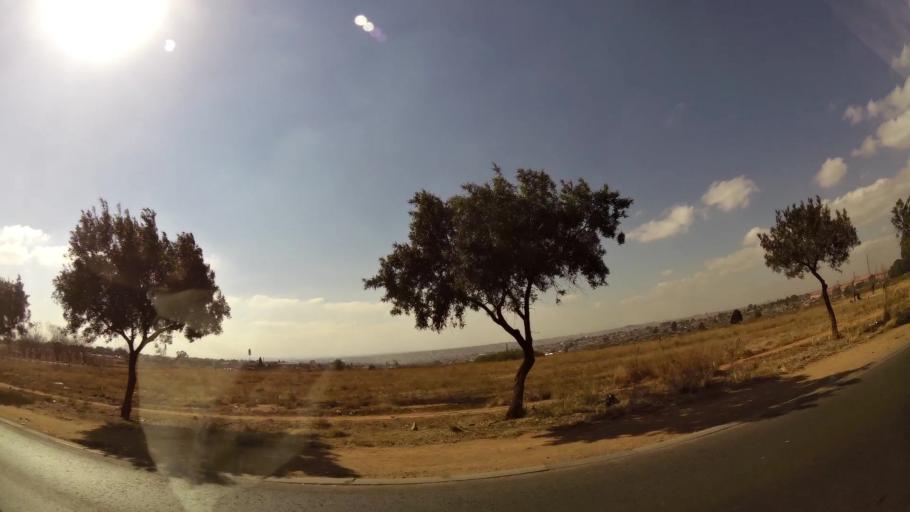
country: ZA
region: Gauteng
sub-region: City of Johannesburg Metropolitan Municipality
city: Midrand
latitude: -26.0262
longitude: 28.1702
